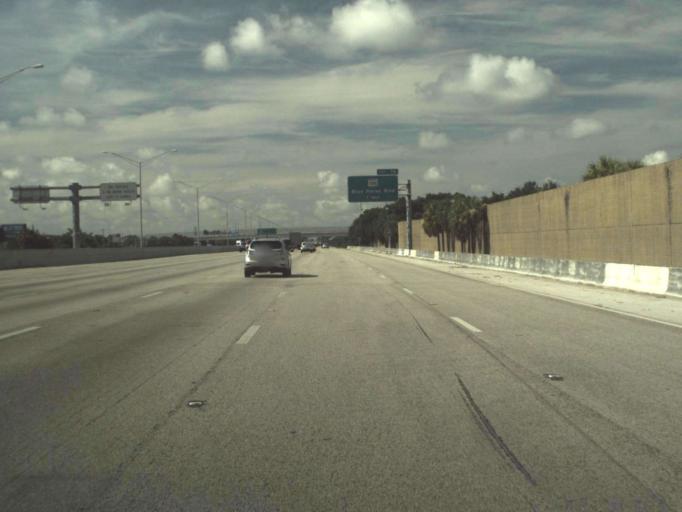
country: US
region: Florida
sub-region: Palm Beach County
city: North Palm Beach
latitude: 26.8028
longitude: -80.0988
